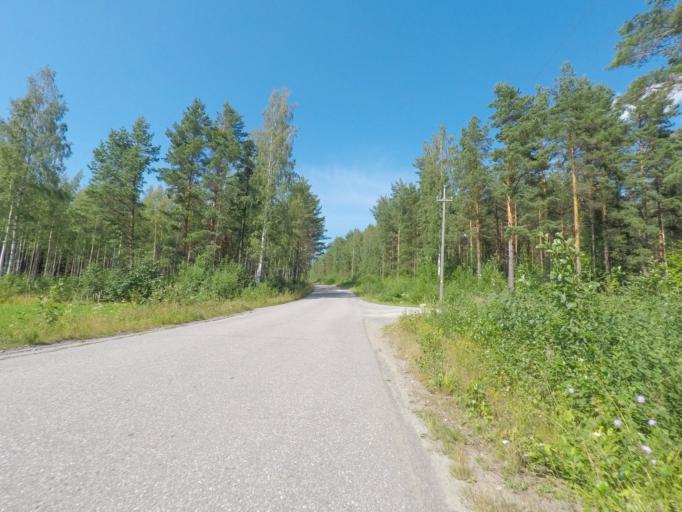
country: FI
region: Southern Savonia
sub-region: Mikkeli
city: Puumala
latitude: 61.4414
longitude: 28.1652
